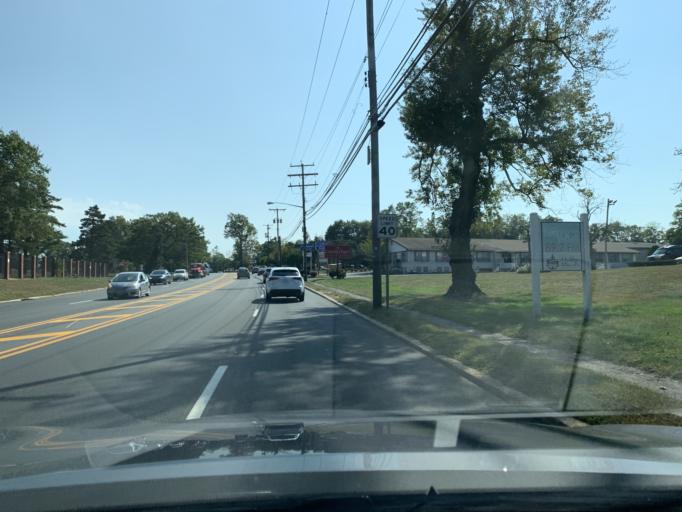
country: US
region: New Jersey
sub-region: Monmouth County
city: Shrewsbury
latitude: 40.3109
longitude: -74.0644
